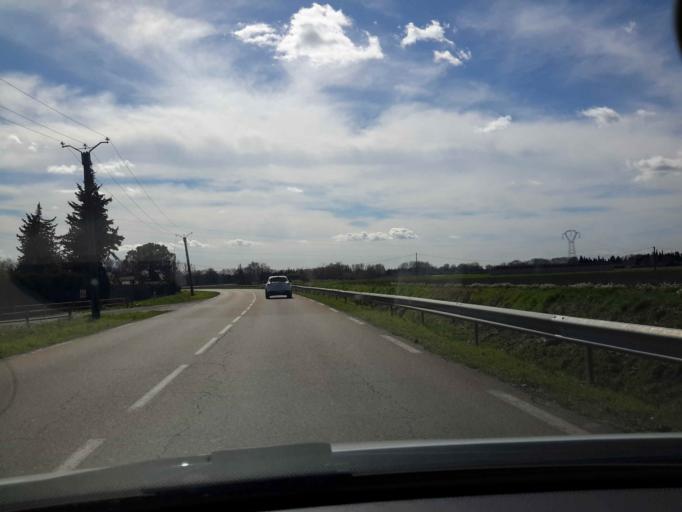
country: FR
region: Languedoc-Roussillon
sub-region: Departement du Gard
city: Caissargues
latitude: 43.7978
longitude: 4.3529
